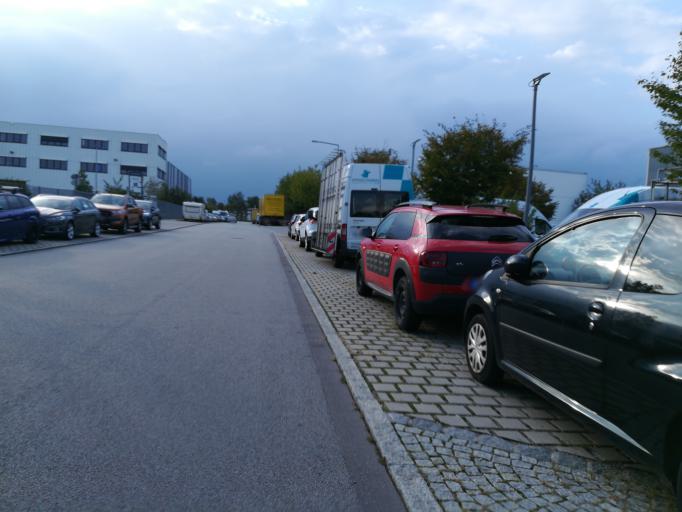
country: DE
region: Bavaria
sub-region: Upper Bavaria
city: Hebertshausen
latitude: 48.2581
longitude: 11.4739
